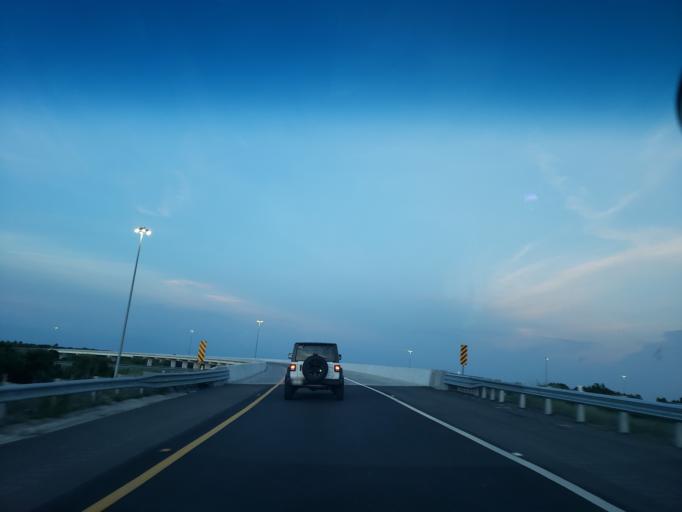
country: US
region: Florida
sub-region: Manatee County
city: Ellenton
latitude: 27.5847
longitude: -82.5195
